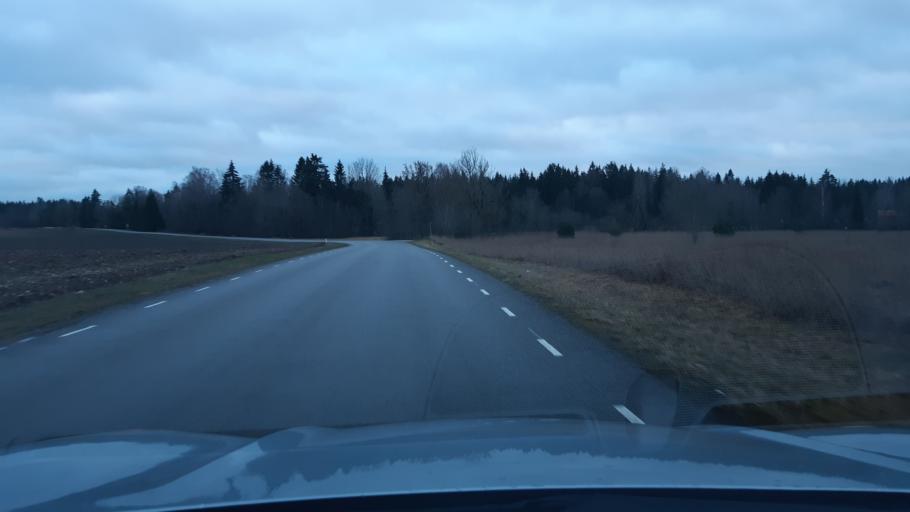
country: EE
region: Harju
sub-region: Saue linn
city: Saue
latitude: 59.2269
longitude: 24.5202
